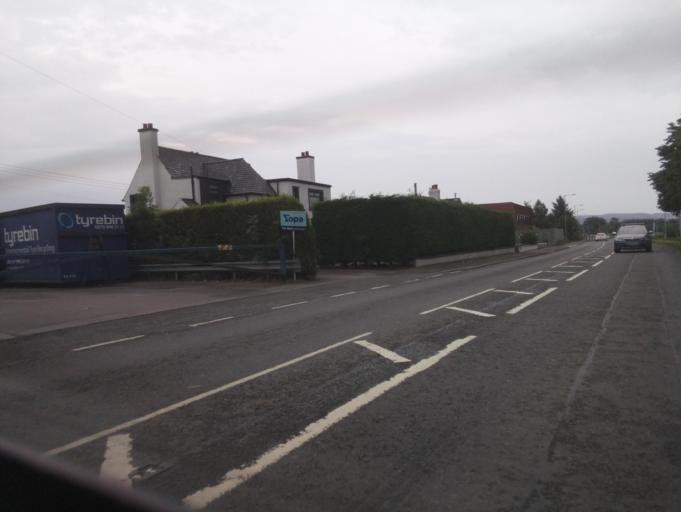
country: GB
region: Scotland
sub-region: Dumfries and Galloway
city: Locharbriggs
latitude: 55.0690
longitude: -3.5651
